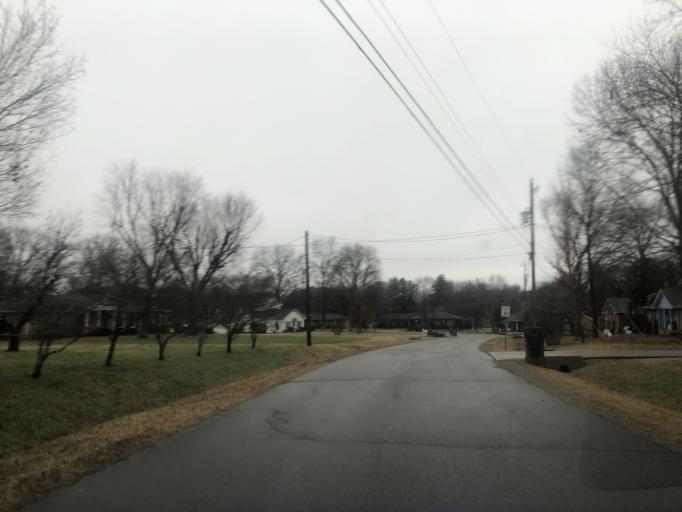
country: US
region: Tennessee
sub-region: Davidson County
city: Belle Meade
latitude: 36.0876
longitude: -86.9522
